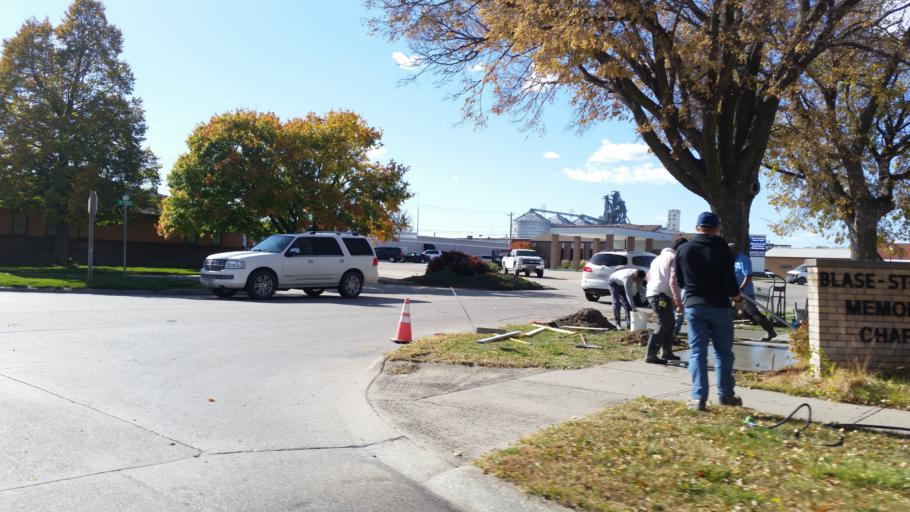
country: US
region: Nebraska
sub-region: Dawson County
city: Gothenburg
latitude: 40.9277
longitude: -100.1590
